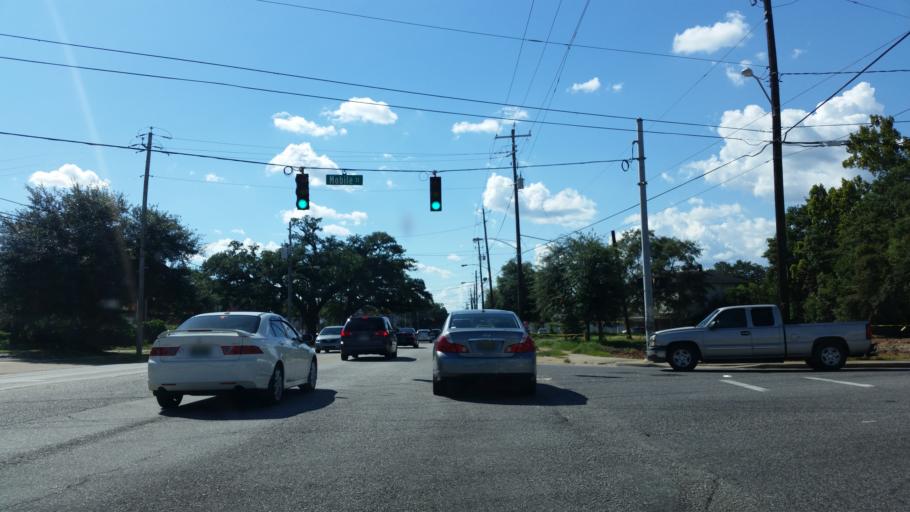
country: US
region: Alabama
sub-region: Mobile County
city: Prichard
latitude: 30.6968
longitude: -88.1036
